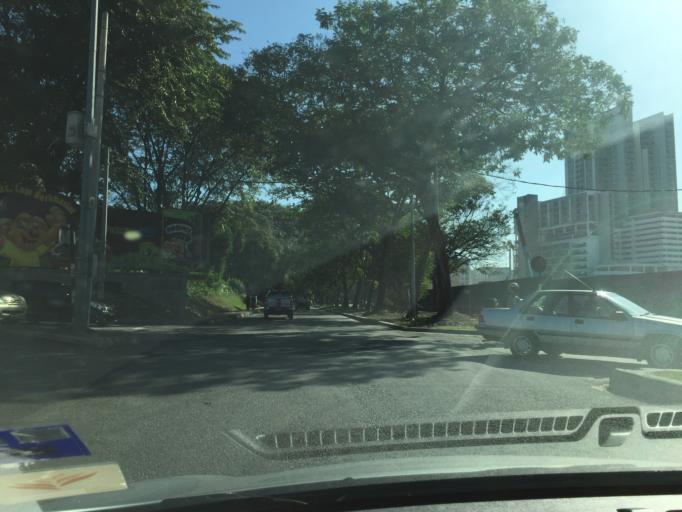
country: MY
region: Selangor
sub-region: Petaling
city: Petaling Jaya
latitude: 3.1185
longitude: 101.6315
